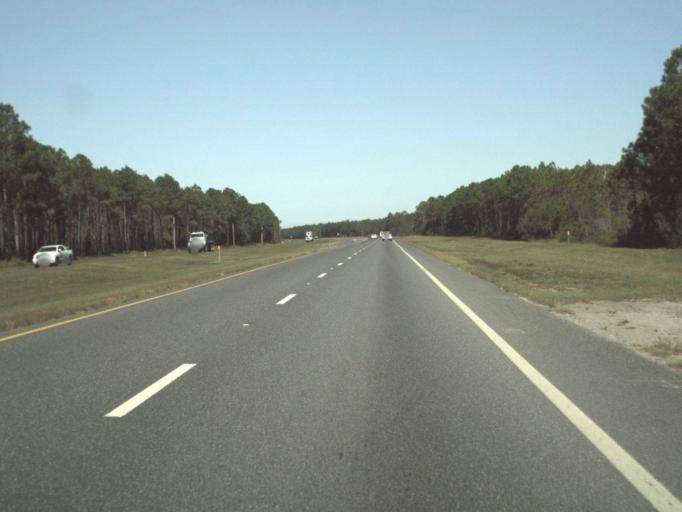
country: US
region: Florida
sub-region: Walton County
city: Seaside
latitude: 30.3257
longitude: -86.0505
